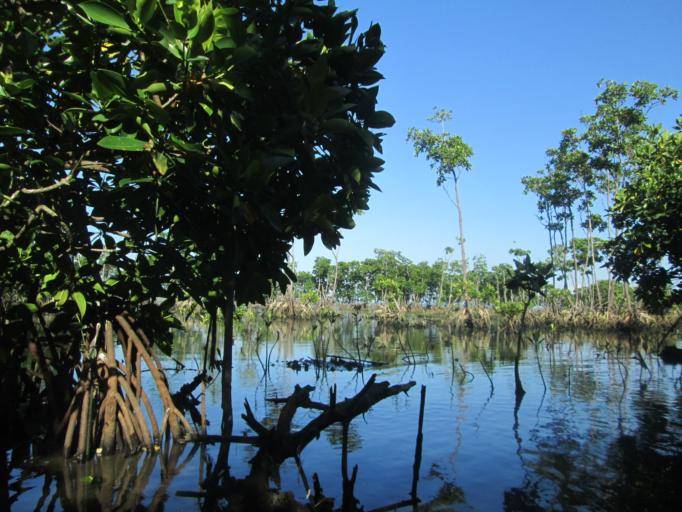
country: PH
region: Ilocos
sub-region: Province of Pangasinan
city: Pangapisan
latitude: 16.2447
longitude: 119.9295
